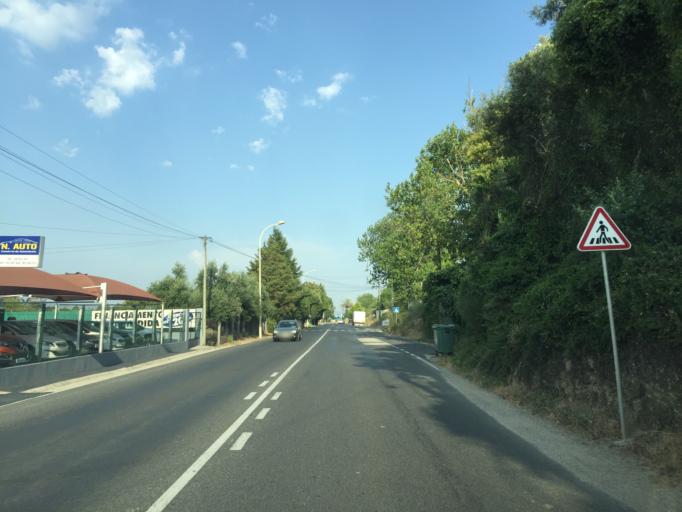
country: PT
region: Santarem
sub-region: Torres Novas
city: Torres Novas
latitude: 39.4759
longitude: -8.5629
